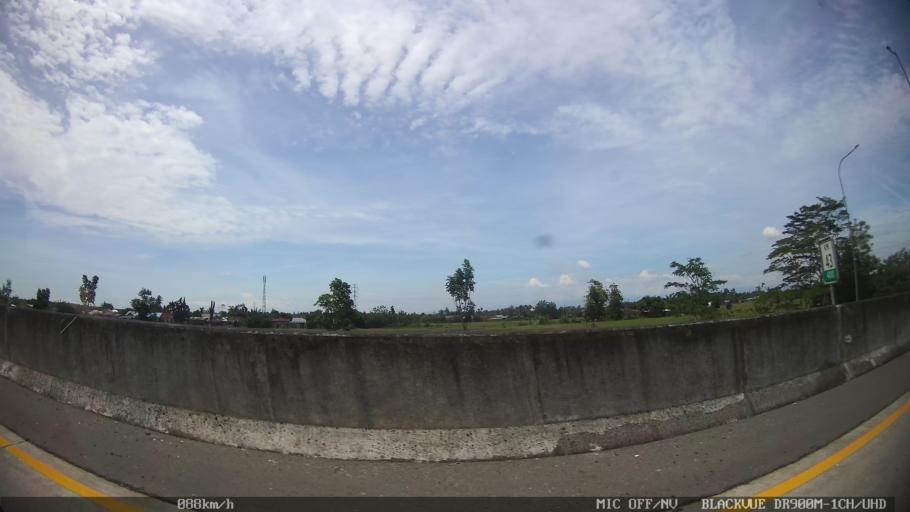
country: ID
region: North Sumatra
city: Percut
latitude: 3.5359
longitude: 98.8597
